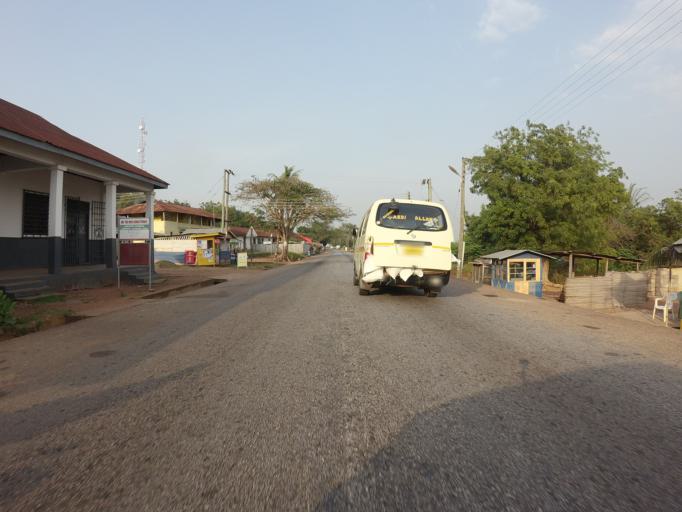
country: GH
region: Volta
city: Ho
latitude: 6.5420
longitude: 0.2882
